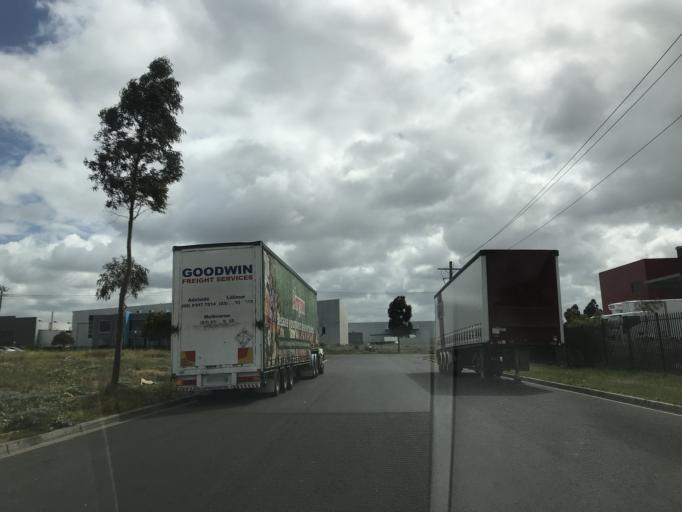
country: AU
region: Victoria
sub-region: Brimbank
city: Derrimut
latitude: -37.7892
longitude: 144.7795
